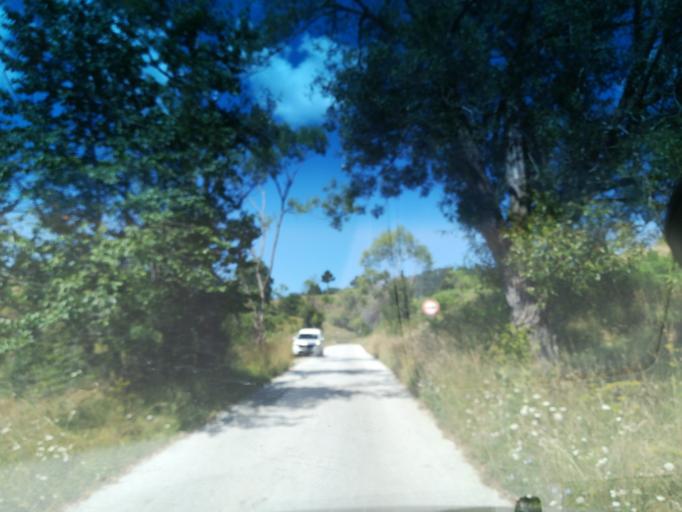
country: BG
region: Smolyan
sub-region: Obshtina Chepelare
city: Chepelare
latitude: 41.6703
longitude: 24.7814
